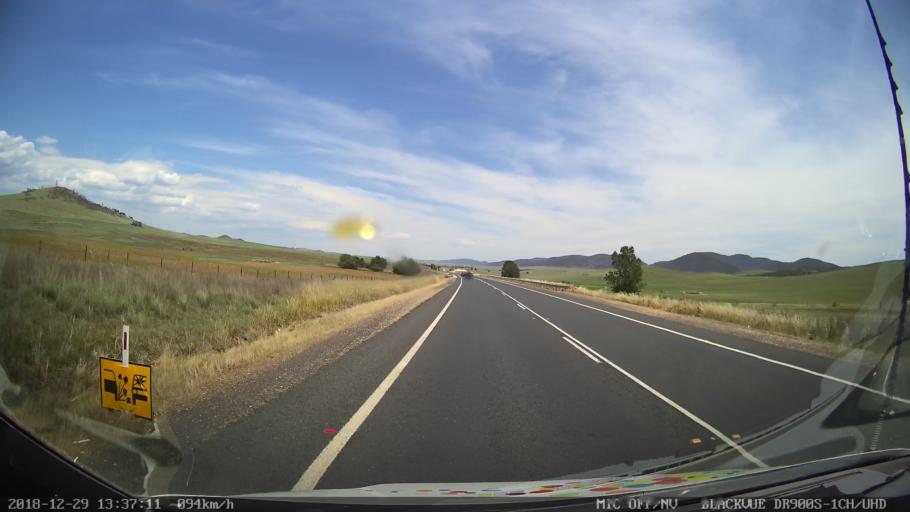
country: AU
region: New South Wales
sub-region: Cooma-Monaro
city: Cooma
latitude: -35.9800
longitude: 149.1372
